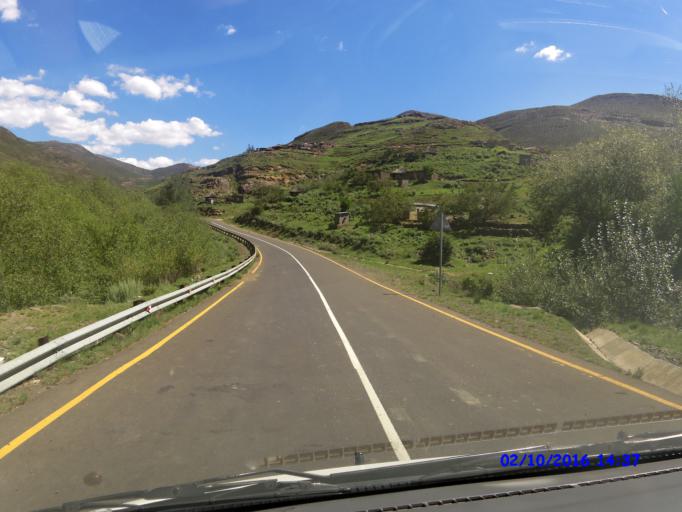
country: LS
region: Maseru
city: Nako
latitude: -29.5048
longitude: 28.0633
